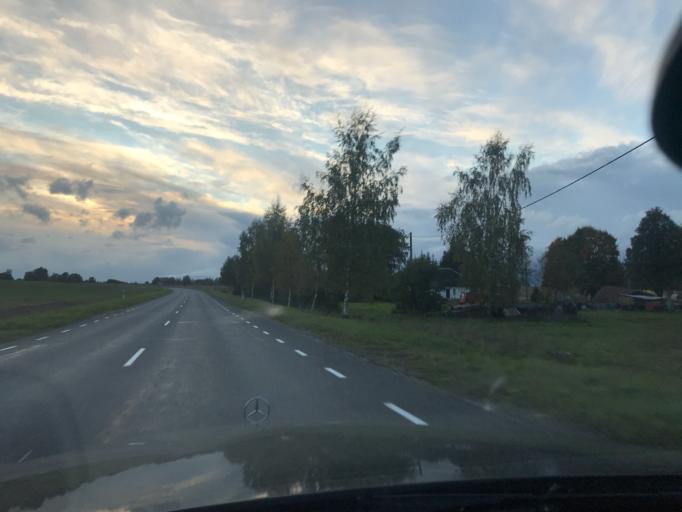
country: EE
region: Valgamaa
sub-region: Torva linn
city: Torva
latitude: 57.9859
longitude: 26.0312
